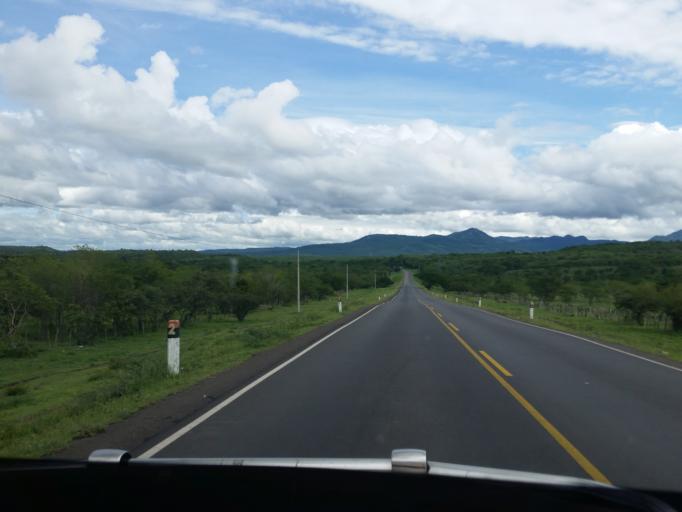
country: NI
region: Matagalpa
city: Ciudad Dario
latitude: 12.6825
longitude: -86.0865
